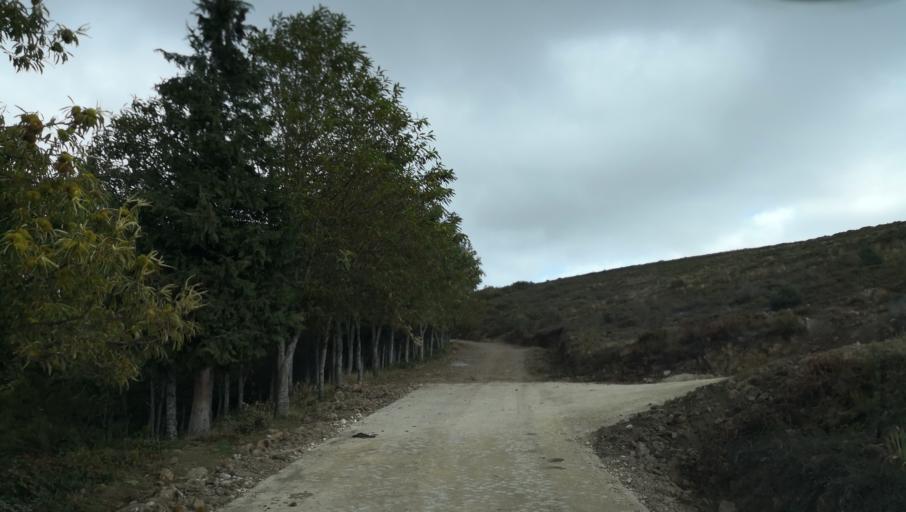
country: PT
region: Vila Real
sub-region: Vila Real
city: Vila Real
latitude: 41.3718
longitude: -7.7930
